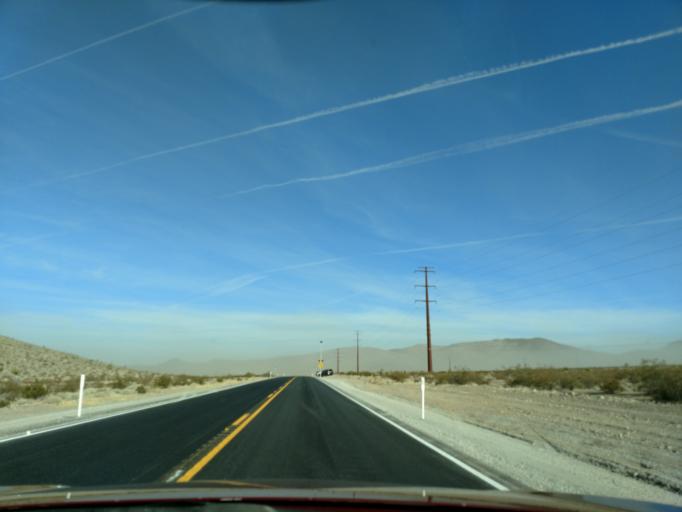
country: US
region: Nevada
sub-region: Nye County
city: Pahrump
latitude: 36.4274
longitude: -116.0710
